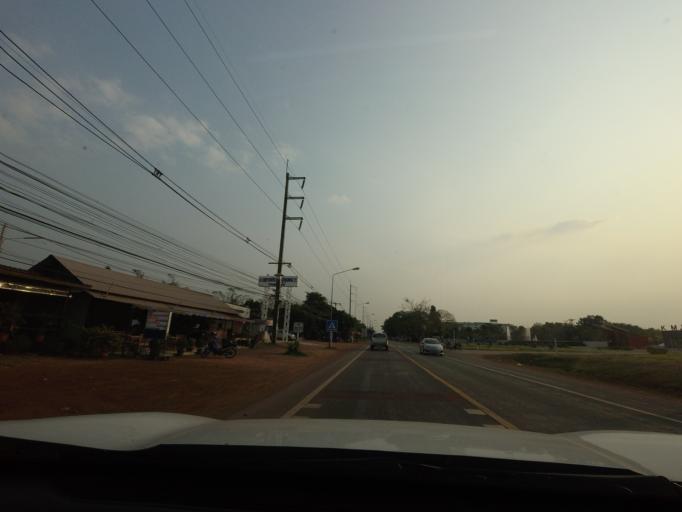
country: TH
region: Nakhon Nayok
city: Pak Phli
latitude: 14.1641
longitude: 101.3657
